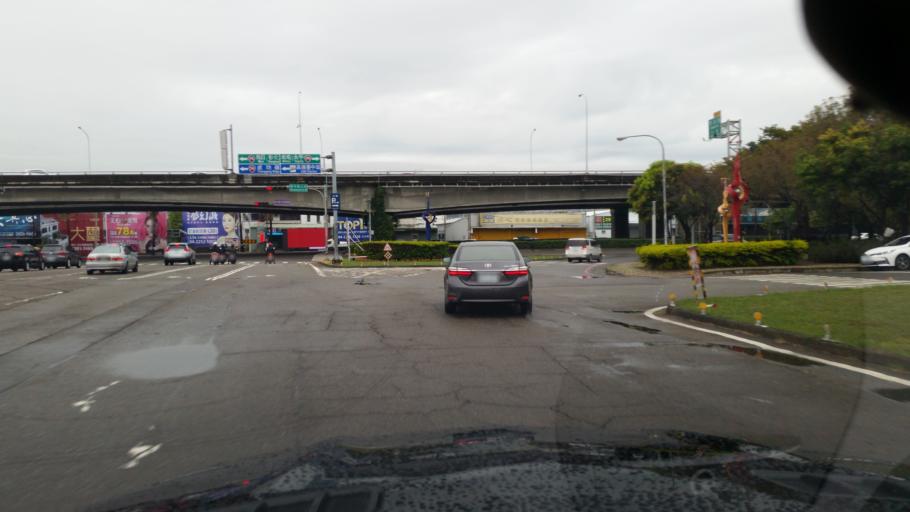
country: TW
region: Taiwan
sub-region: Taichung City
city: Taichung
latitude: 24.1629
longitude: 120.6300
